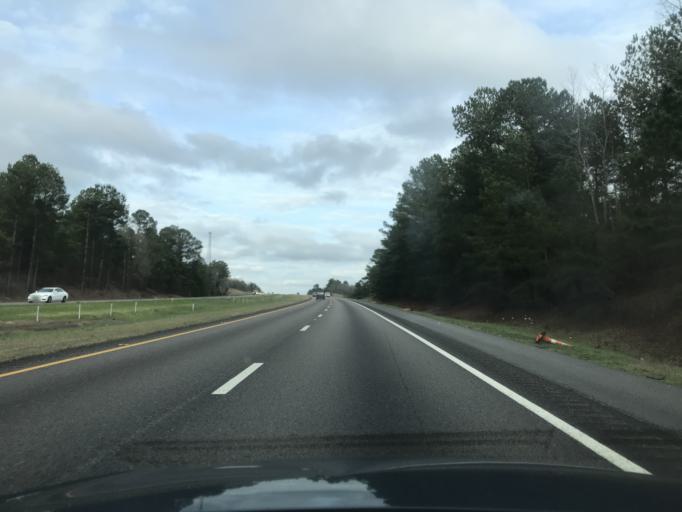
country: US
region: South Carolina
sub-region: Edgefield County
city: Murphys Estates
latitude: 33.5849
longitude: -81.8863
